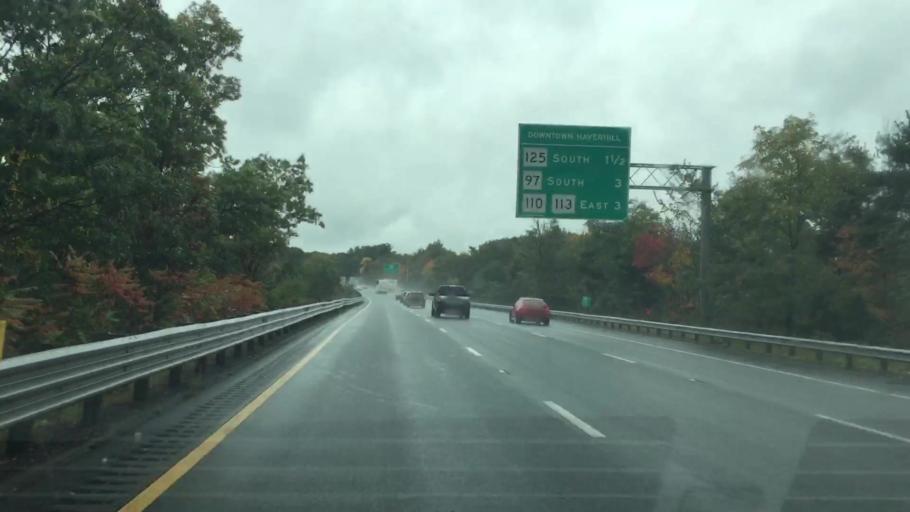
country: US
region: Massachusetts
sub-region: Essex County
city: Haverhill
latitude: 42.8054
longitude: -71.0666
